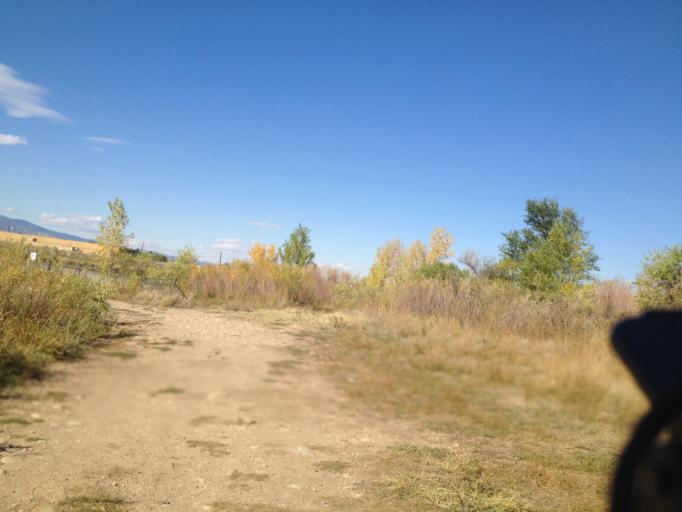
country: US
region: Colorado
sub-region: Boulder County
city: Boulder
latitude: 39.9806
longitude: -105.2294
